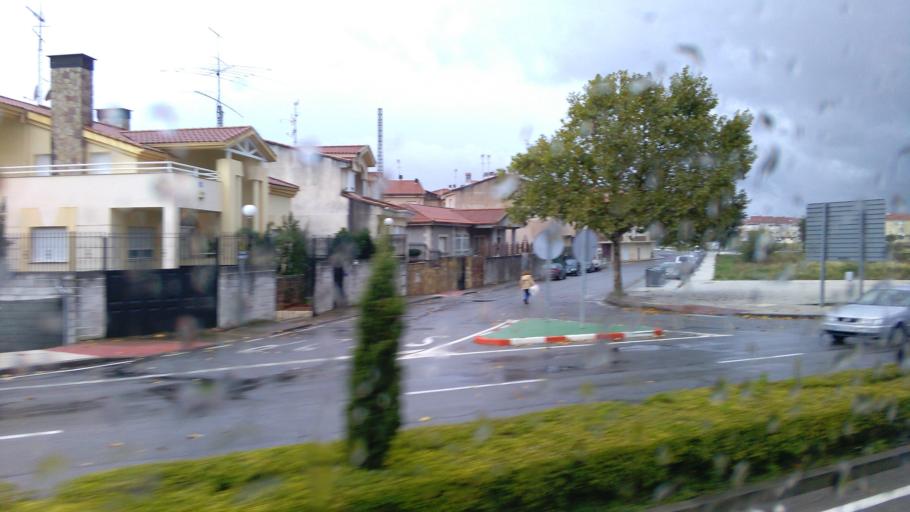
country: ES
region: Extremadura
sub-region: Provincia de Caceres
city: Navalmoral de la Mata
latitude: 39.8923
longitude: -5.5301
